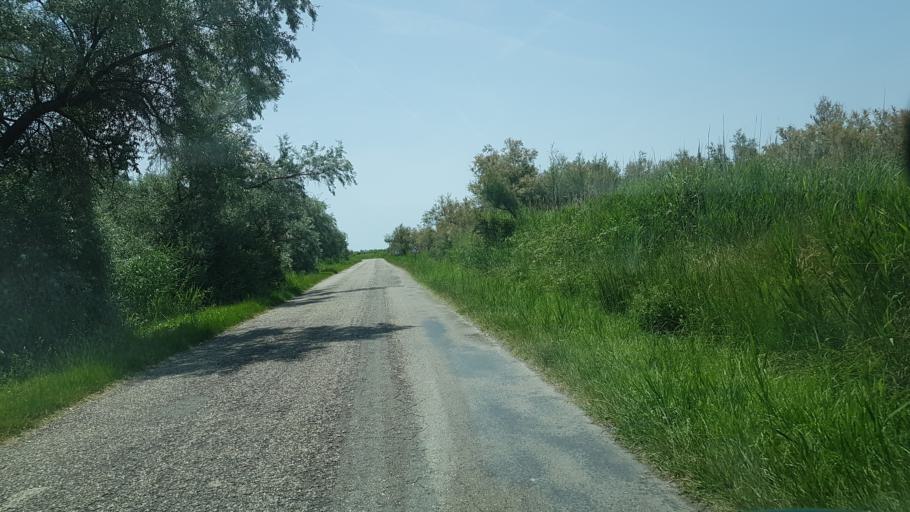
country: FR
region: Provence-Alpes-Cote d'Azur
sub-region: Departement des Bouches-du-Rhone
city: Arles
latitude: 43.5554
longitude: 4.6254
